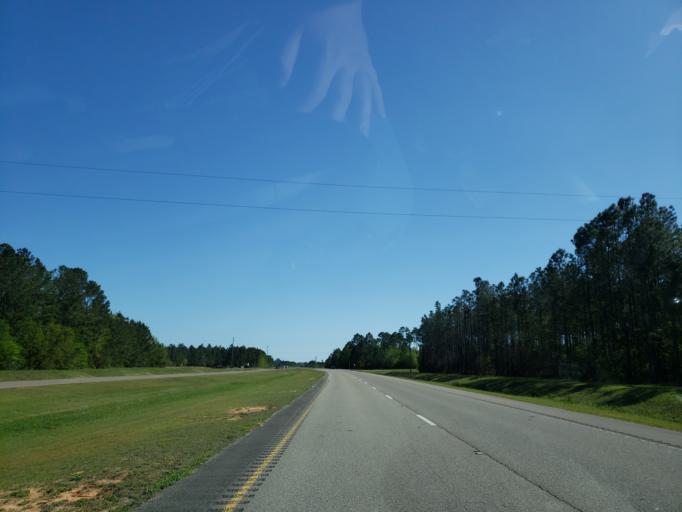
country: US
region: Mississippi
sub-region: Harrison County
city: West Gulfport
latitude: 30.4742
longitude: -89.0288
